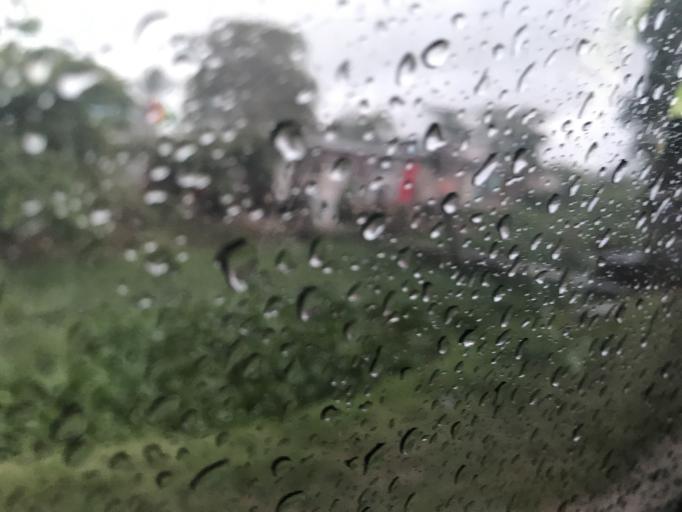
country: GY
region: Demerara-Mahaica
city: Georgetown
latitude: 6.8068
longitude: -58.1162
